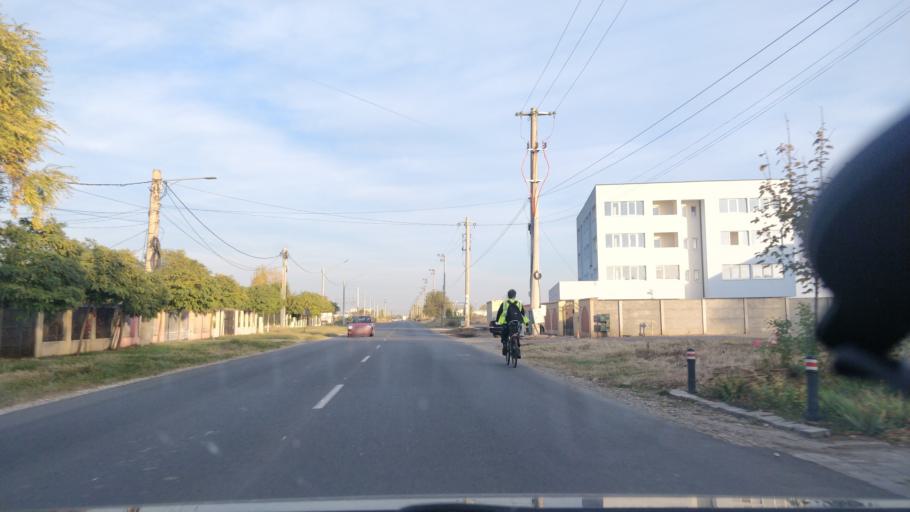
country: RO
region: Ilfov
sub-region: Comuna Ciorogarla
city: Ciorogarla
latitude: 44.4415
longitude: 25.9054
